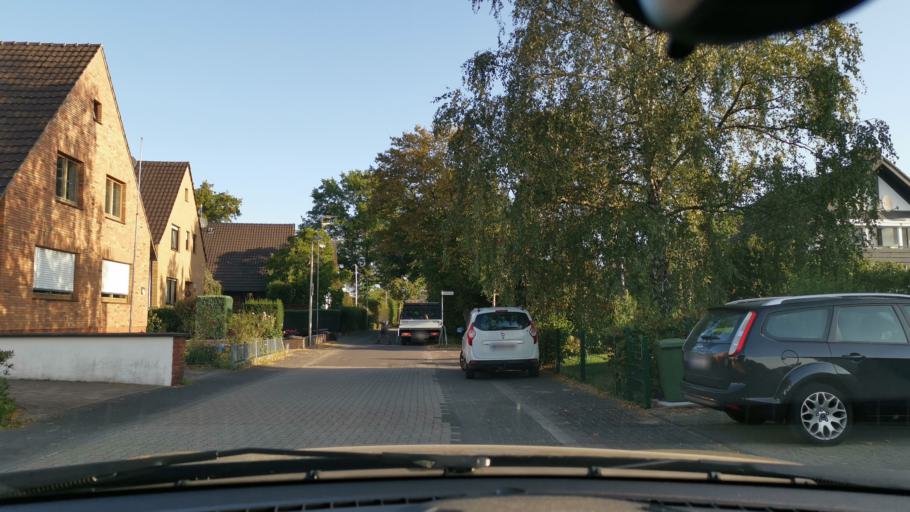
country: DE
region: North Rhine-Westphalia
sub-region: Regierungsbezirk Dusseldorf
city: Rommerskirchen
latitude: 51.0996
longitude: 6.7216
